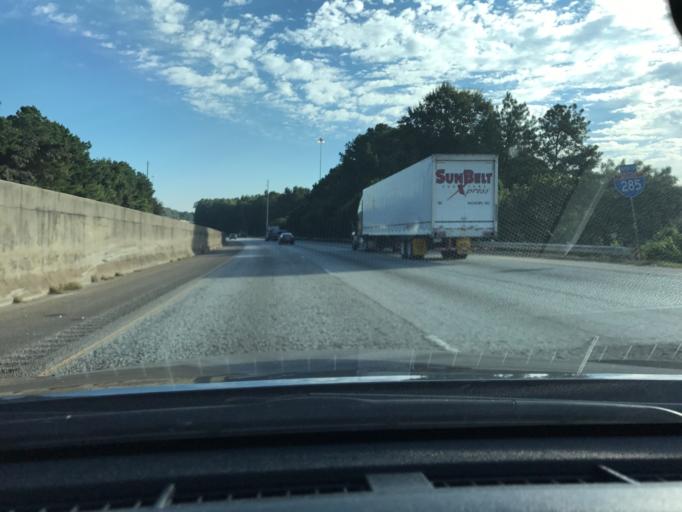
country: US
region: Georgia
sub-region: DeKalb County
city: Panthersville
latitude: 33.7150
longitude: -84.2406
